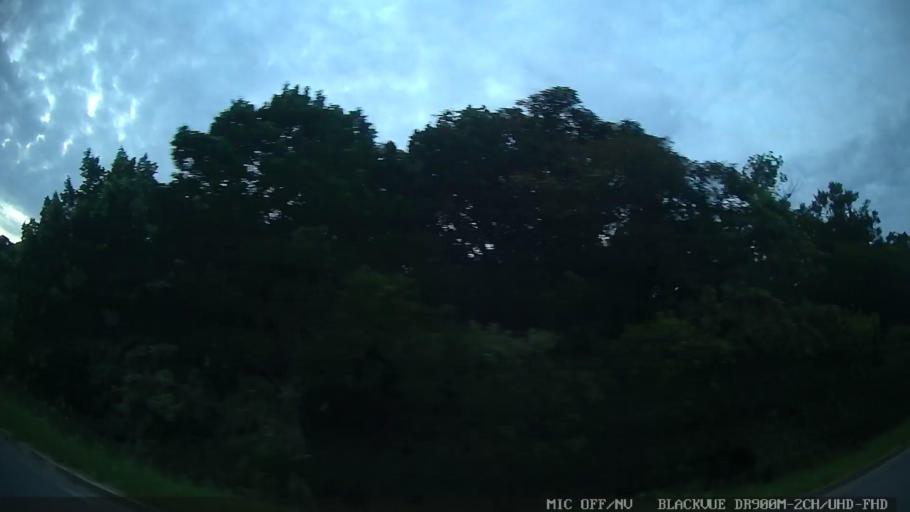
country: BR
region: Sao Paulo
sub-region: Itanhaem
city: Itanhaem
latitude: -24.1937
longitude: -46.8350
